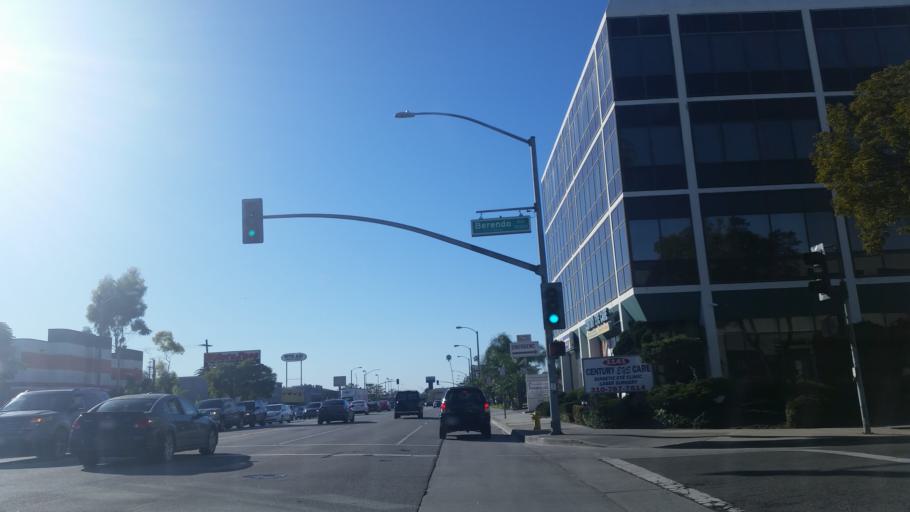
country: US
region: California
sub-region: Los Angeles County
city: Gardena
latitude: 33.8926
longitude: -118.2937
